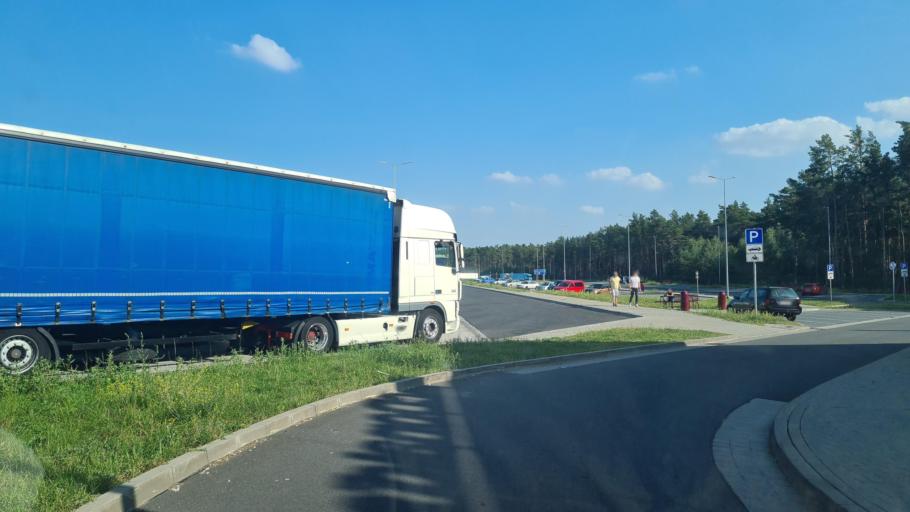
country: DE
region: Brandenburg
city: Michendorf
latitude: 52.3016
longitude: 13.0172
